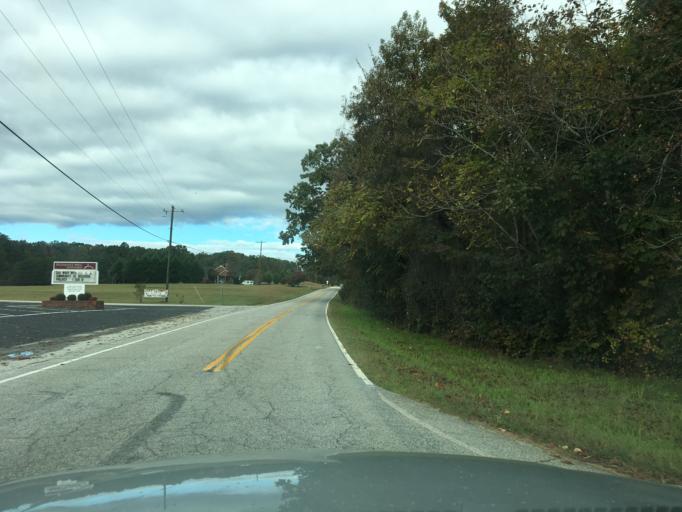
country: US
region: South Carolina
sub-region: Greenville County
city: Tigerville
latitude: 35.0640
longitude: -82.2853
